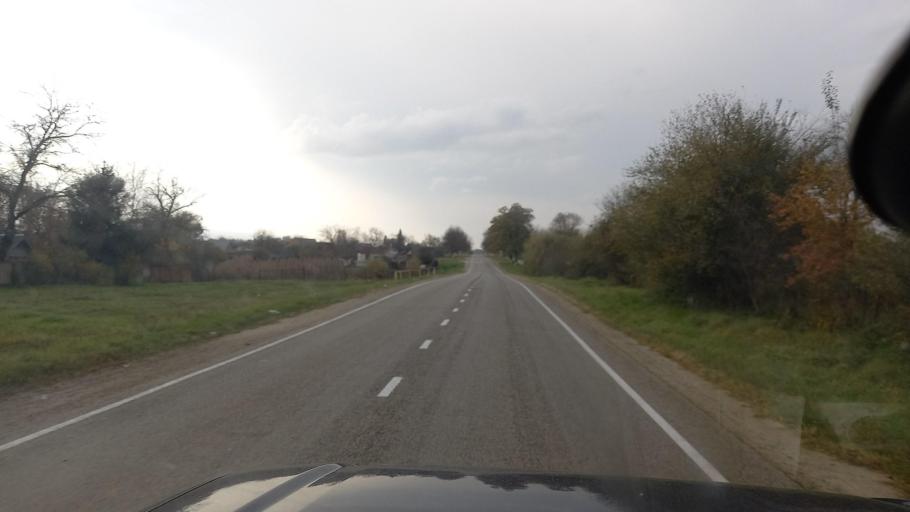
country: RU
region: Krasnodarskiy
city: Gubskaya
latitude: 44.3184
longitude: 40.6181
